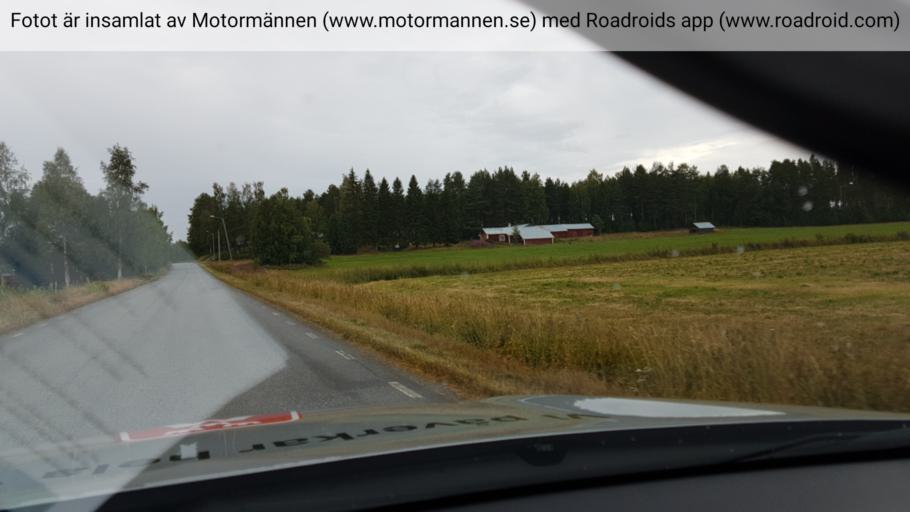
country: SE
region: Norrbotten
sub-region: Bodens Kommun
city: Boden
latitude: 65.8225
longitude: 21.5601
